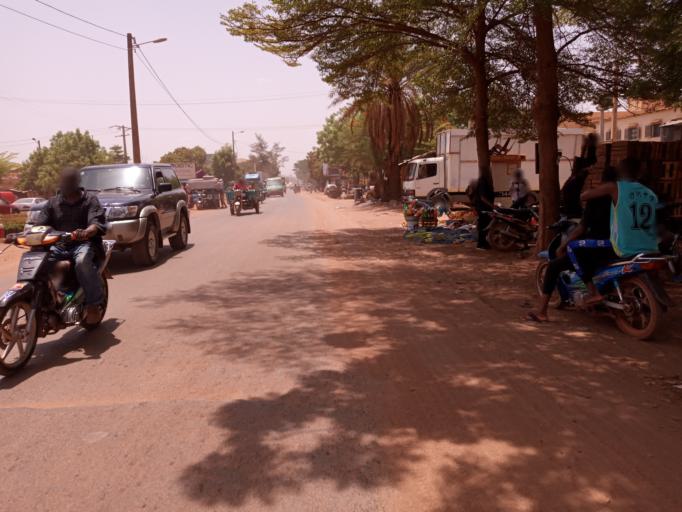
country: ML
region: Bamako
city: Bamako
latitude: 12.6484
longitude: -7.9738
